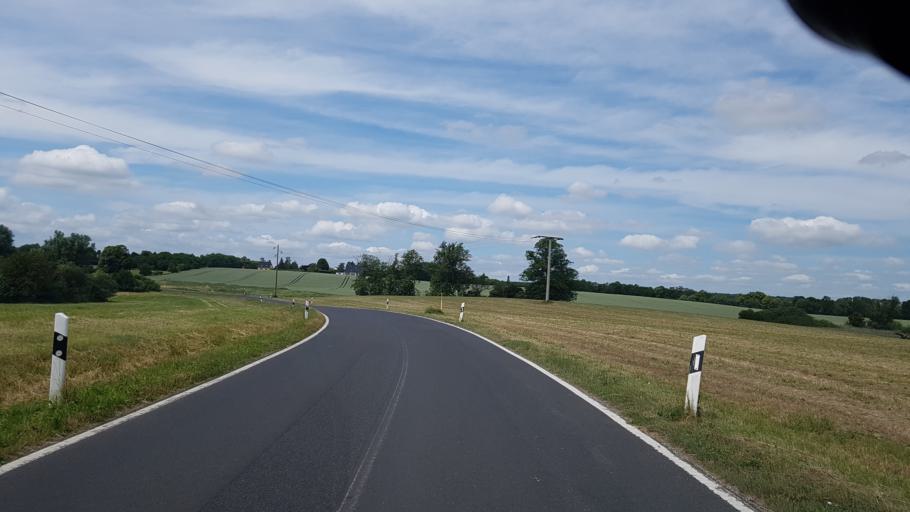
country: DE
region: Mecklenburg-Vorpommern
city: Strasburg
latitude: 53.4552
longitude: 13.8129
